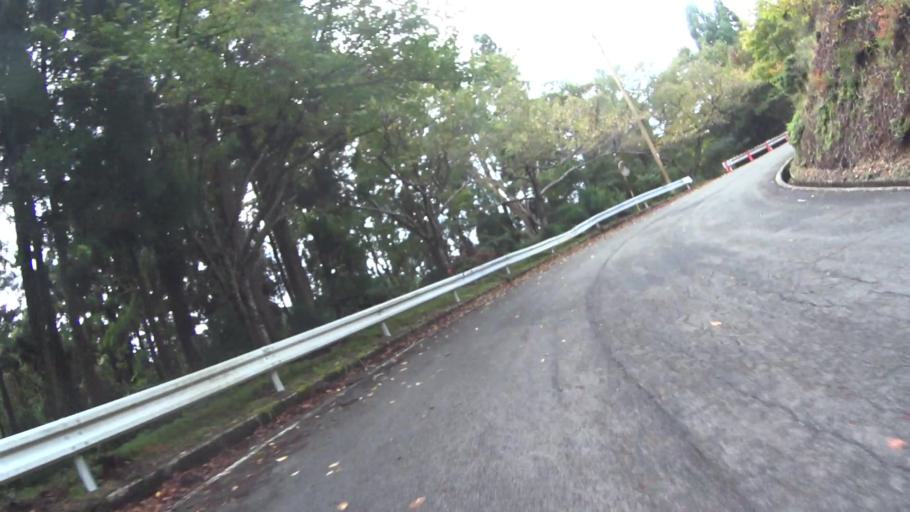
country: JP
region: Shiga Prefecture
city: Kitahama
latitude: 35.2744
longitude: 135.7316
